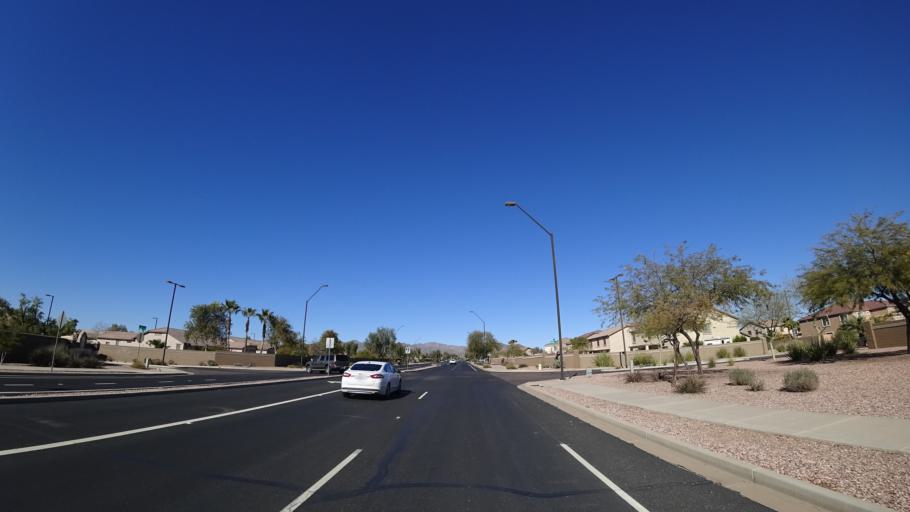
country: US
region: Arizona
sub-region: Maricopa County
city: Buckeye
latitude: 33.4294
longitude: -112.5390
